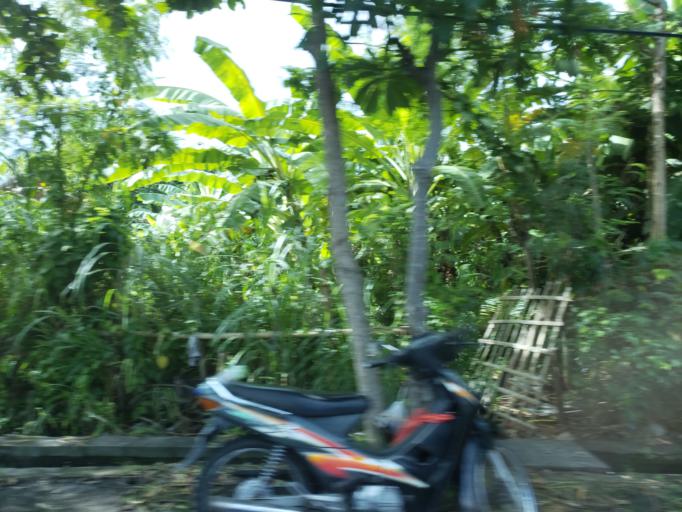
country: ID
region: Bali
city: Kuta
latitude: -8.6832
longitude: 115.1758
